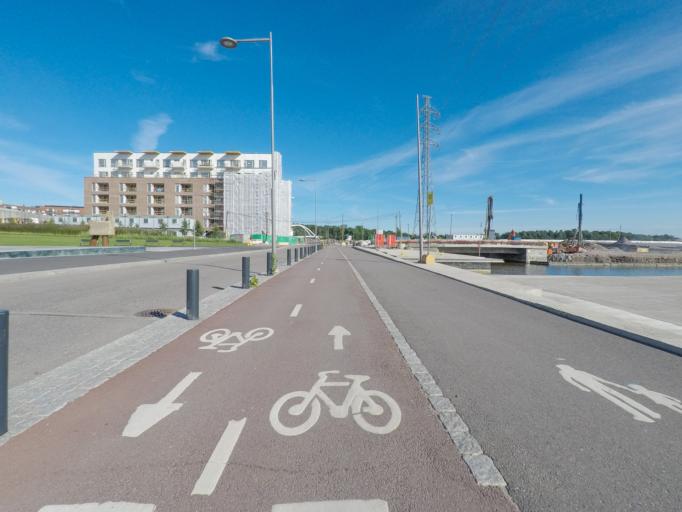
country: FI
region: Uusimaa
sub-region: Helsinki
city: Helsinki
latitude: 60.1837
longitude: 24.9755
